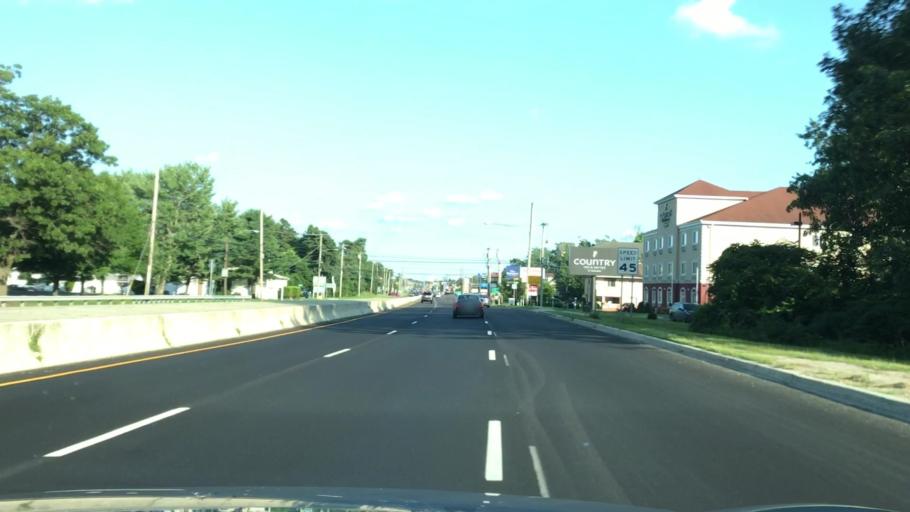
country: US
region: New Jersey
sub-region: Atlantic County
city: Absecon
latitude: 39.4514
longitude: -74.5361
